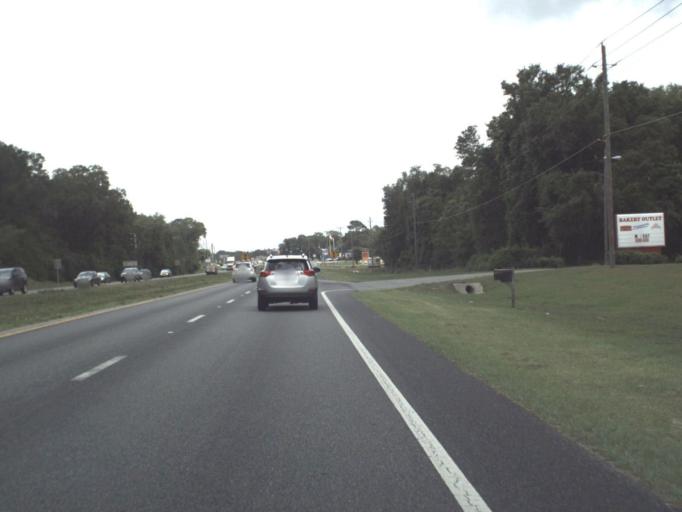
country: US
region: Florida
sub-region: Sumter County
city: The Villages
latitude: 28.9854
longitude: -81.9900
